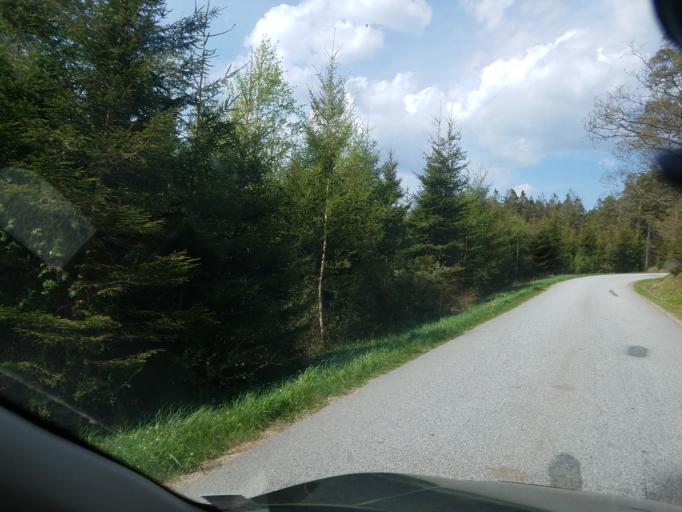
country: SE
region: Vaestra Goetaland
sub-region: Orust
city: Henan
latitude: 58.2838
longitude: 11.5794
